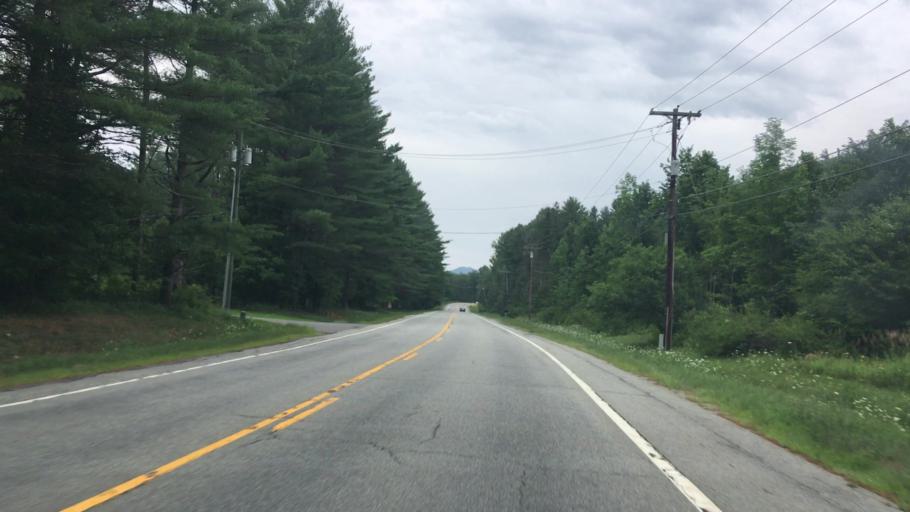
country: US
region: New York
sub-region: Essex County
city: Lake Placid
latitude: 44.2693
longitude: -73.7908
